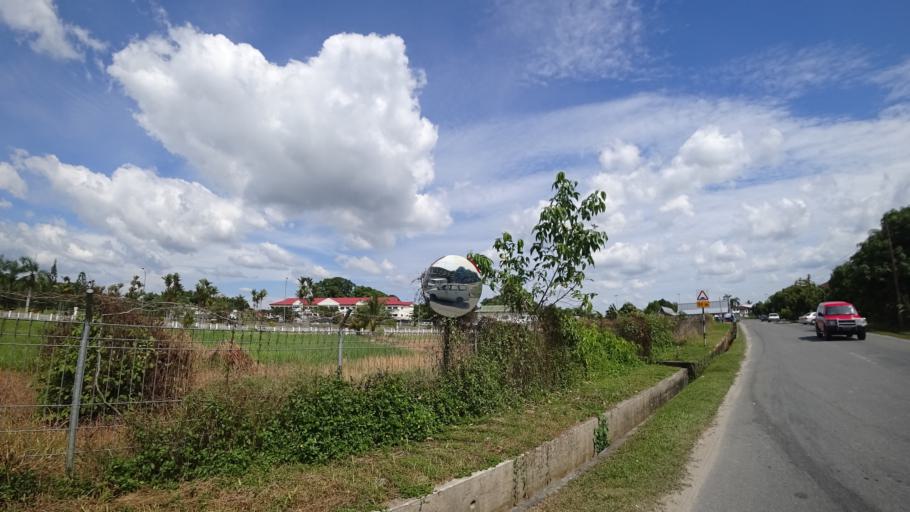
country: BN
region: Brunei and Muara
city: Bandar Seri Begawan
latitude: 4.8961
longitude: 114.8493
